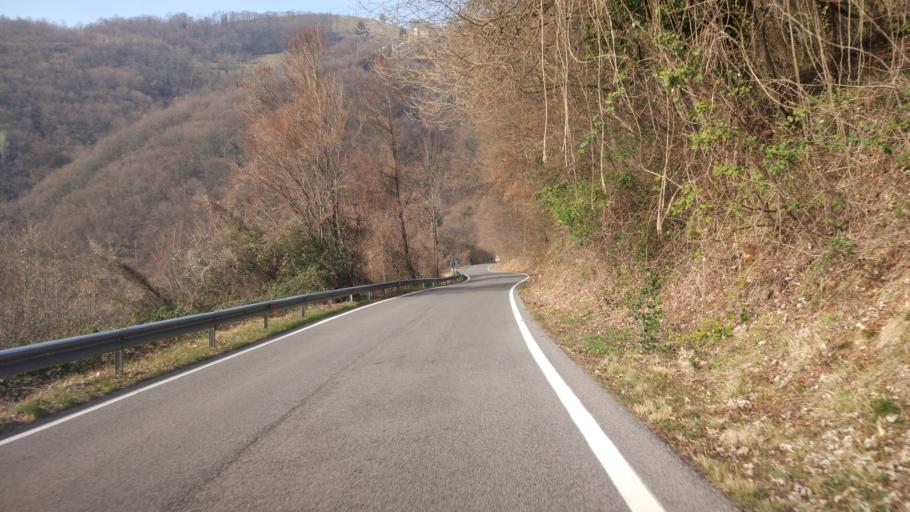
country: IT
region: Veneto
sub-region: Provincia di Verona
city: Selva di Progno
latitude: 45.6063
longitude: 11.1696
